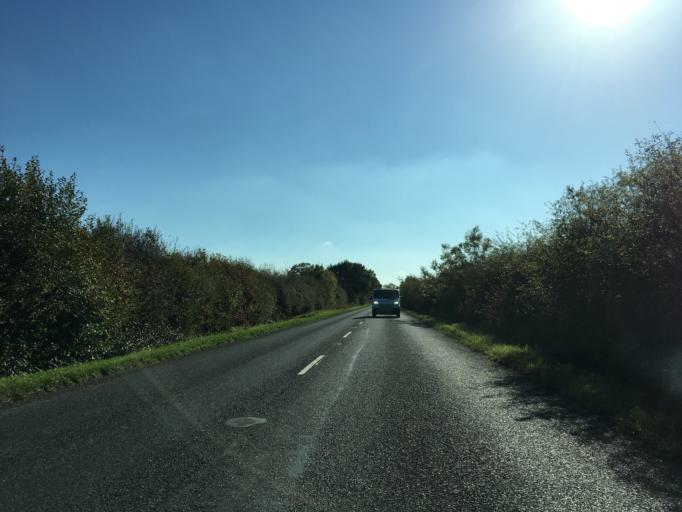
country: GB
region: England
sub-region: South Gloucestershire
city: Wickwar
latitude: 51.5735
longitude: -2.3986
